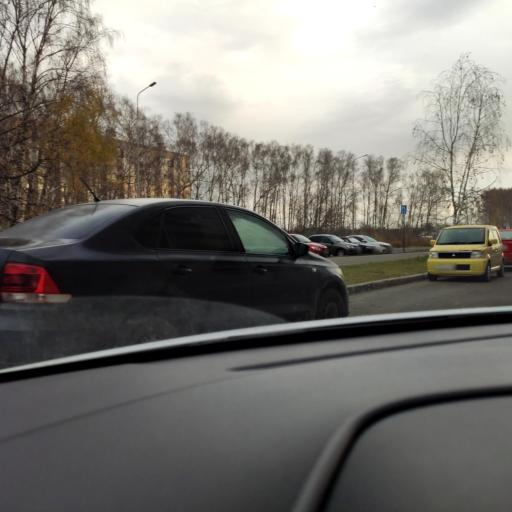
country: RU
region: Tatarstan
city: Osinovo
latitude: 55.8684
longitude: 48.8822
